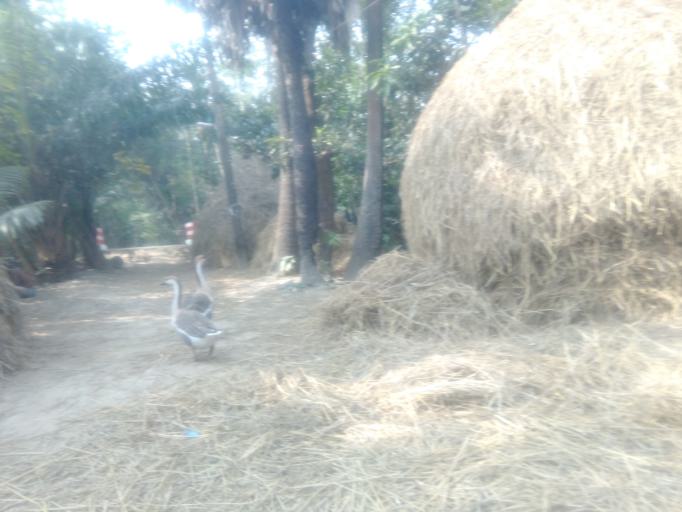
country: IN
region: Tripura
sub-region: West Tripura
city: Sonamura
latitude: 23.3203
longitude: 91.2772
